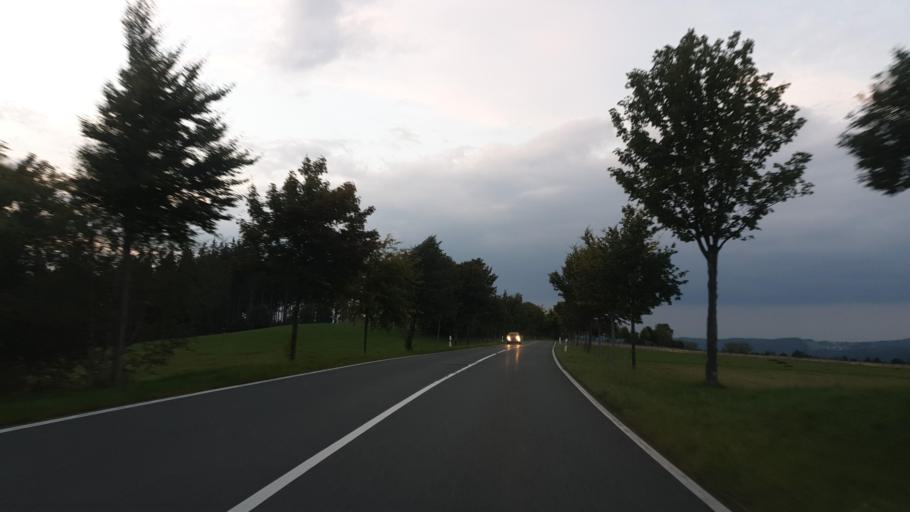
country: DE
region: Saxony
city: Eibenstock
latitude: 50.4805
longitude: 12.6095
